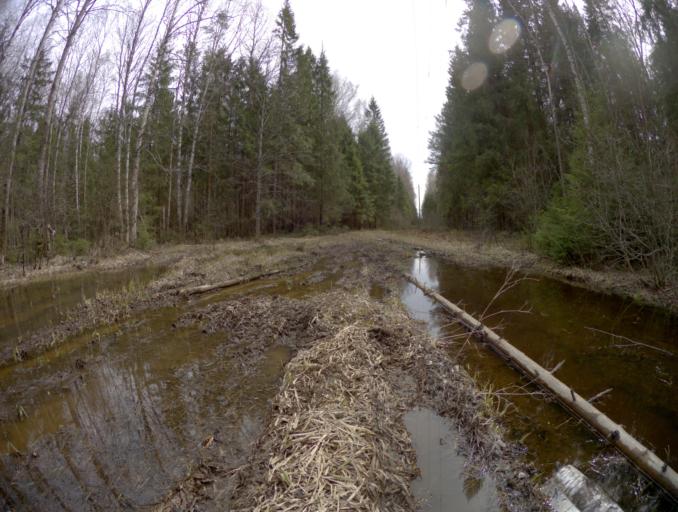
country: RU
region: Vladimir
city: Raduzhnyy
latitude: 55.8832
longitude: 40.2046
